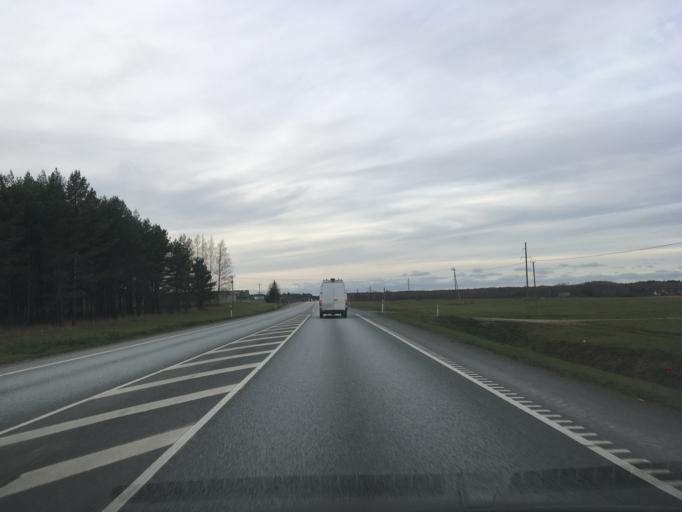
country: EE
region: Ida-Virumaa
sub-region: Kohtla-Jaerve linn
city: Kohtla-Jarve
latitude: 59.4081
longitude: 27.3177
